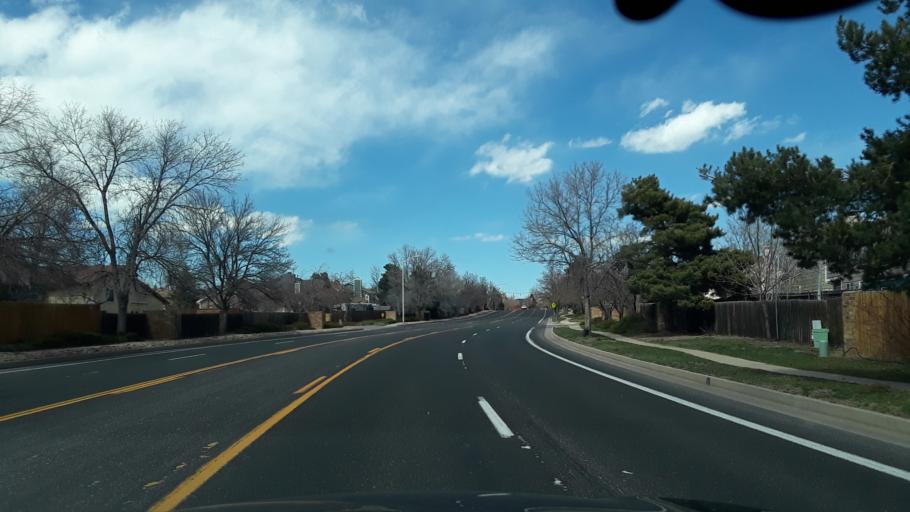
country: US
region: Colorado
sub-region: El Paso County
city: Black Forest
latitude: 38.9539
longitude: -104.7512
